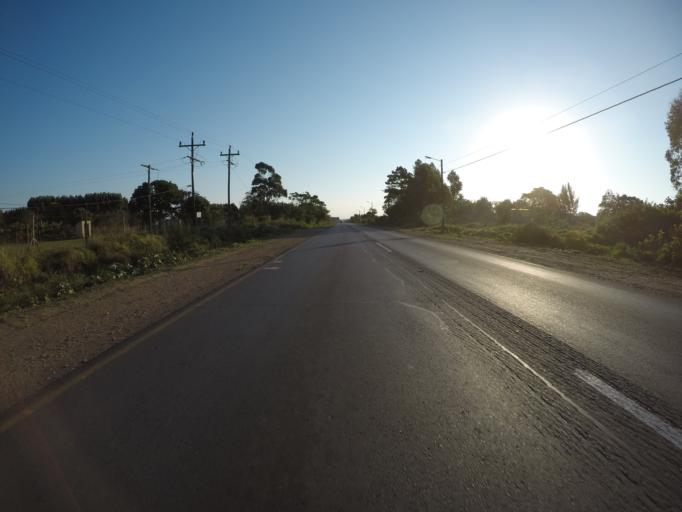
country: ZA
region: KwaZulu-Natal
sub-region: uThungulu District Municipality
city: KwaMbonambi
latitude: -28.6830
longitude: 32.2023
